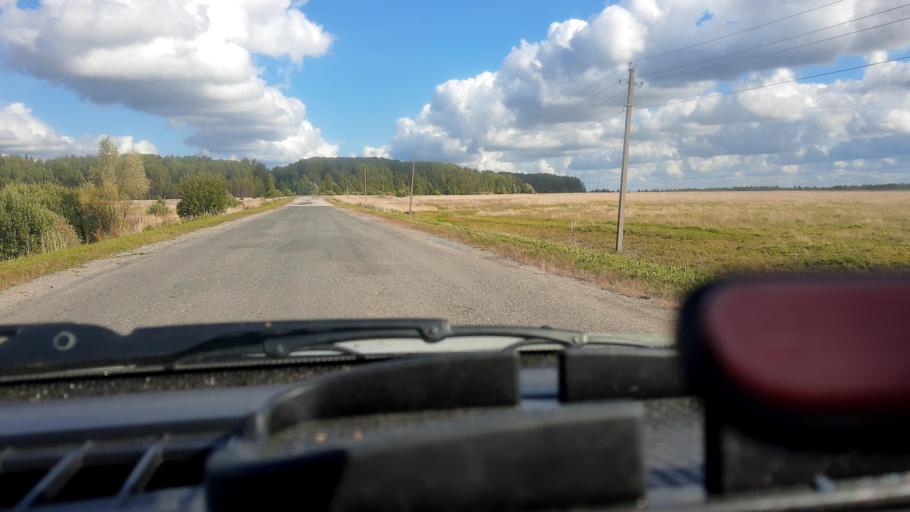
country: RU
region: Mariy-El
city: Kilemary
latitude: 56.9390
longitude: 46.6554
